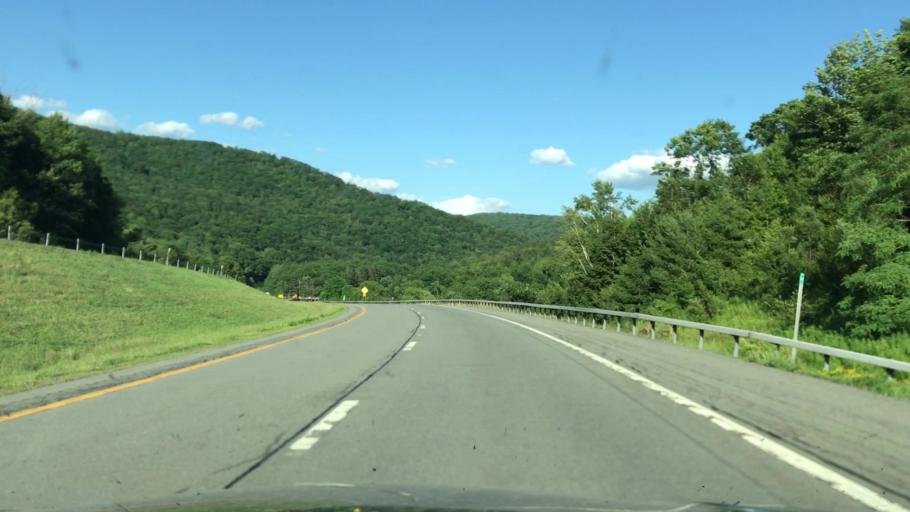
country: US
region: New York
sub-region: Sullivan County
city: Livingston Manor
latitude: 41.9510
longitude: -74.9775
